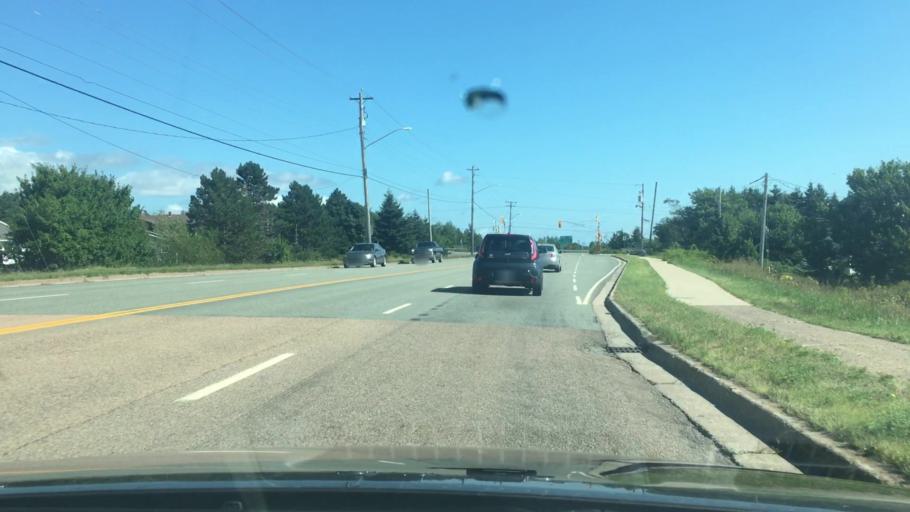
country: CA
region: Nova Scotia
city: Port Hawkesbury
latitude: 45.6129
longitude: -61.3468
